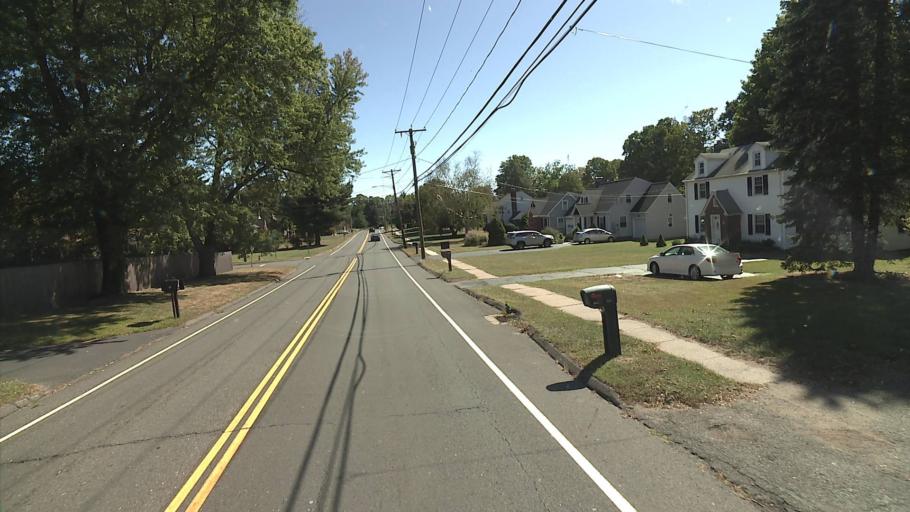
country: US
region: Connecticut
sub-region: New Haven County
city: Cheshire Village
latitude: 41.5124
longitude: -72.9201
